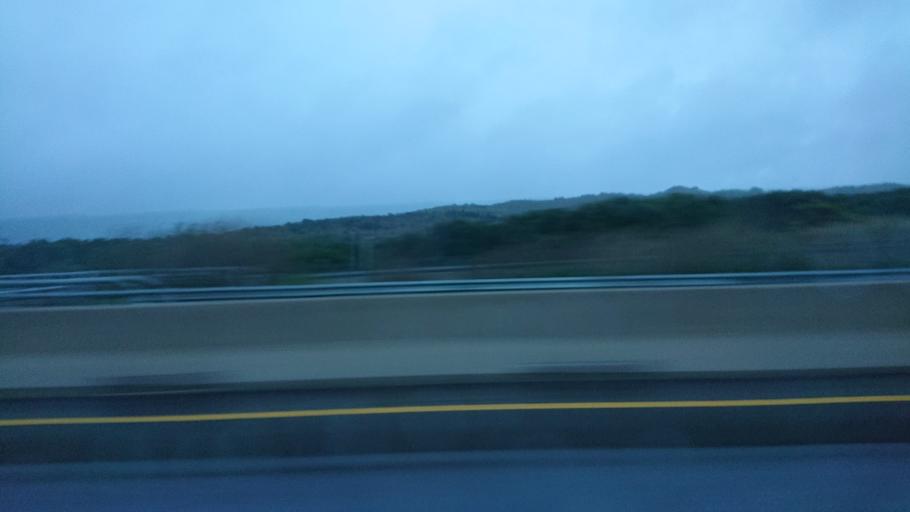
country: TW
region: Taiwan
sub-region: Miaoli
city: Miaoli
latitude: 24.5517
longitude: 120.7072
